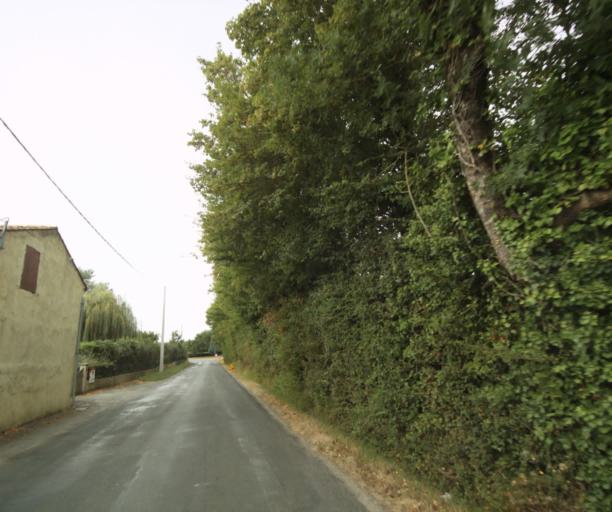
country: FR
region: Poitou-Charentes
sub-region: Departement de la Charente-Maritime
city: Tonnay-Charente
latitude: 45.9566
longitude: -0.8782
